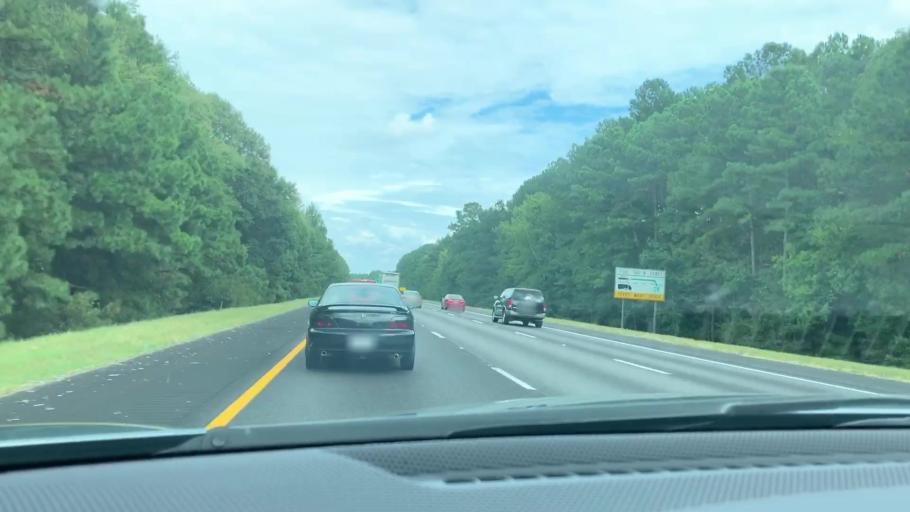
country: US
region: Georgia
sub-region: Chatham County
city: Pooler
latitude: 32.1595
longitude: -81.2266
